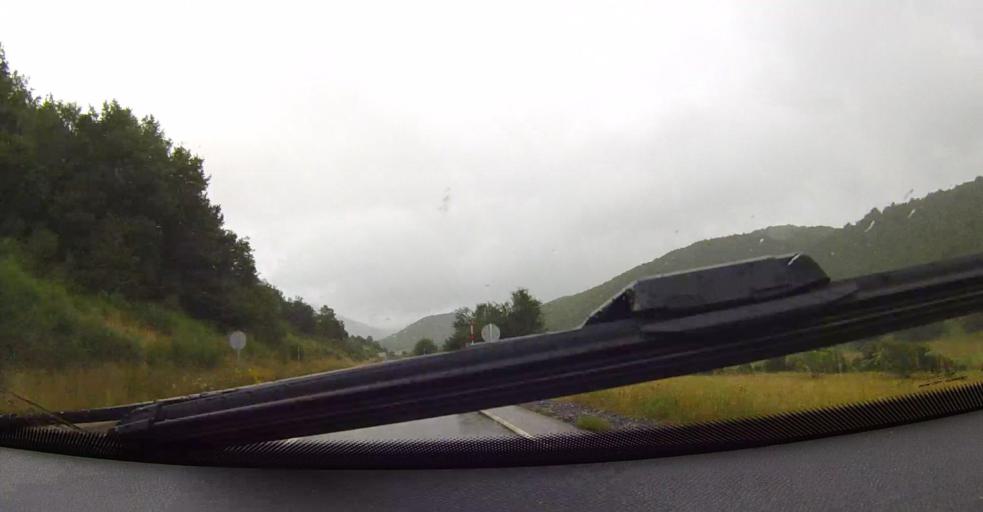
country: ES
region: Castille and Leon
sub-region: Provincia de Leon
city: Marana
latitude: 43.0693
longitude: -5.1787
